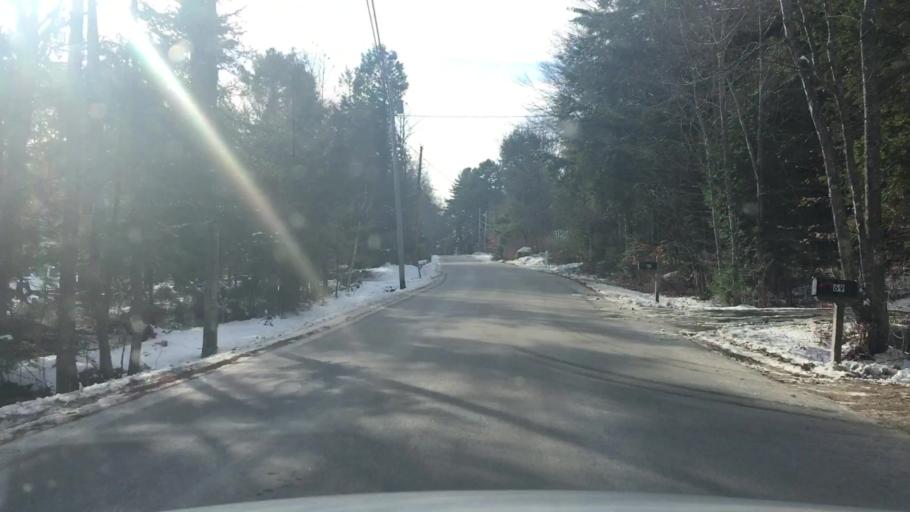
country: US
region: Maine
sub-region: Cumberland County
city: Freeport
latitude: 43.8894
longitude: -70.0866
